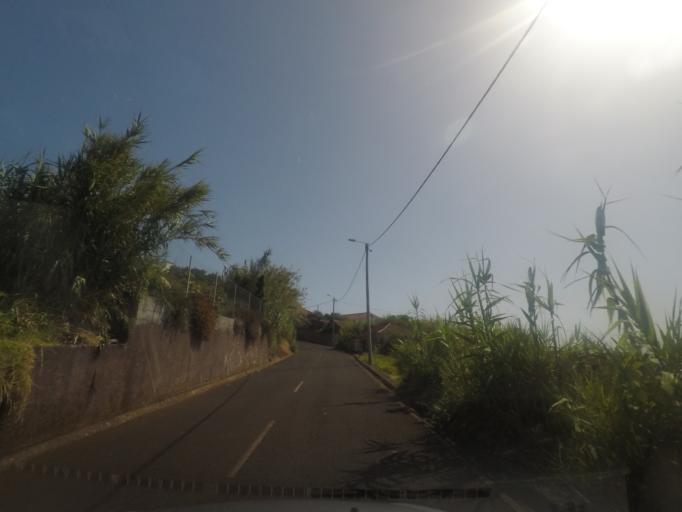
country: PT
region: Madeira
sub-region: Calheta
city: Faja da Ovelha
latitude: 32.8317
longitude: -17.2321
